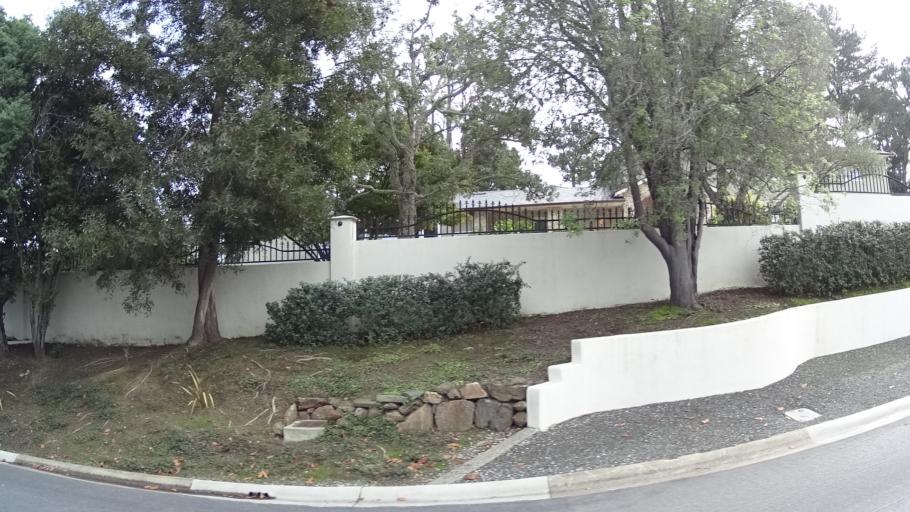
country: US
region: California
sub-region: San Mateo County
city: Hillsborough
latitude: 37.5707
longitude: -122.3859
